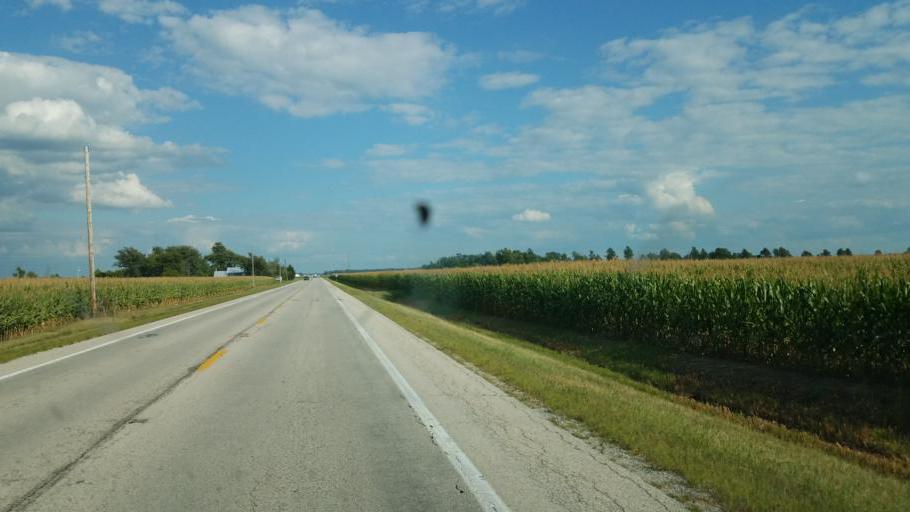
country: US
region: Ohio
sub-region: Wood County
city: Pemberville
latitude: 41.3544
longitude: -83.4699
